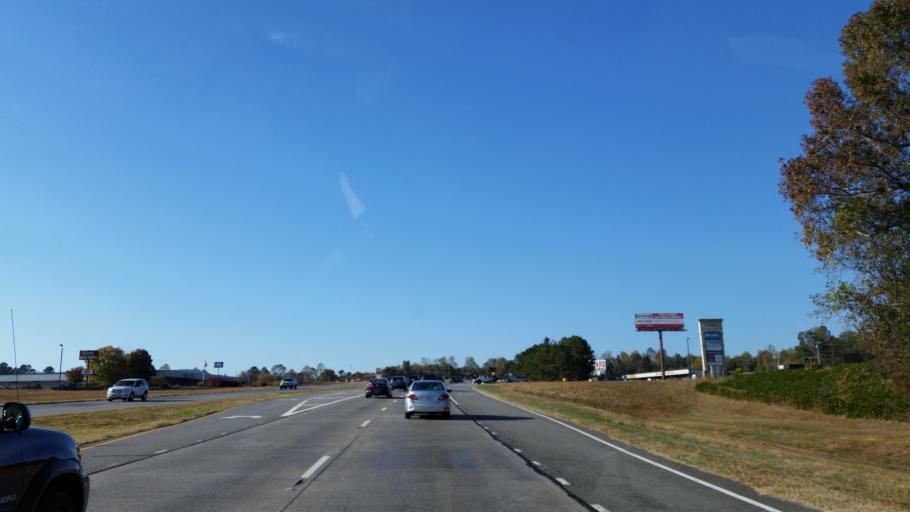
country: US
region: Georgia
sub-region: Pickens County
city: Jasper
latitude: 34.4747
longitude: -84.4645
